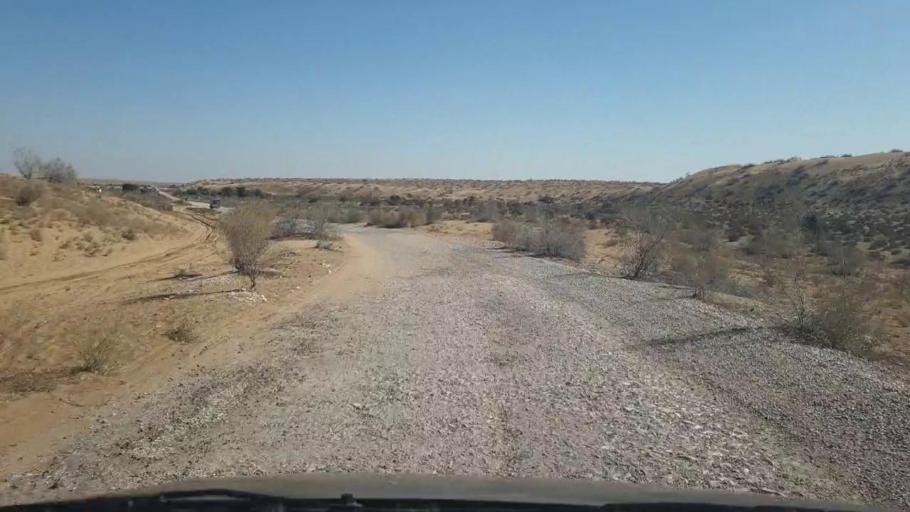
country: PK
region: Sindh
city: Bozdar
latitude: 27.0134
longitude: 68.7389
